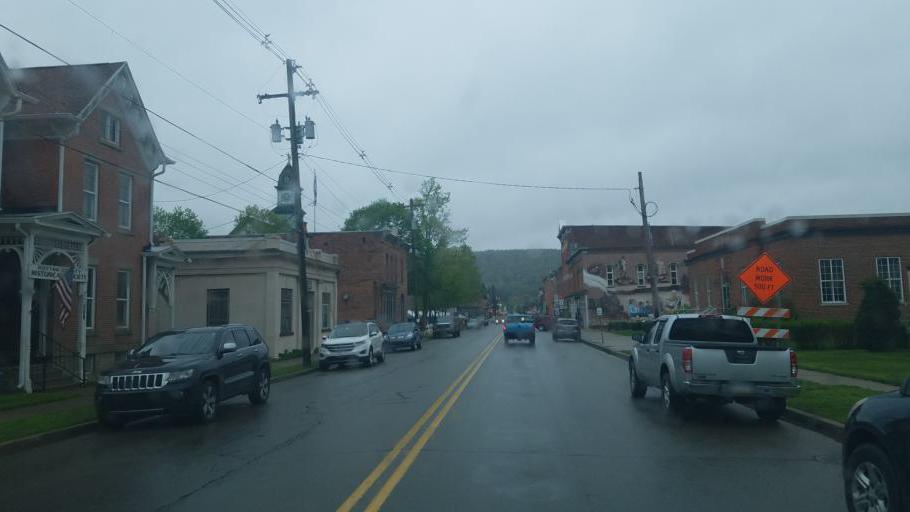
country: US
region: Pennsylvania
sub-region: Potter County
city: Coudersport
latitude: 41.7763
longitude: -78.0209
